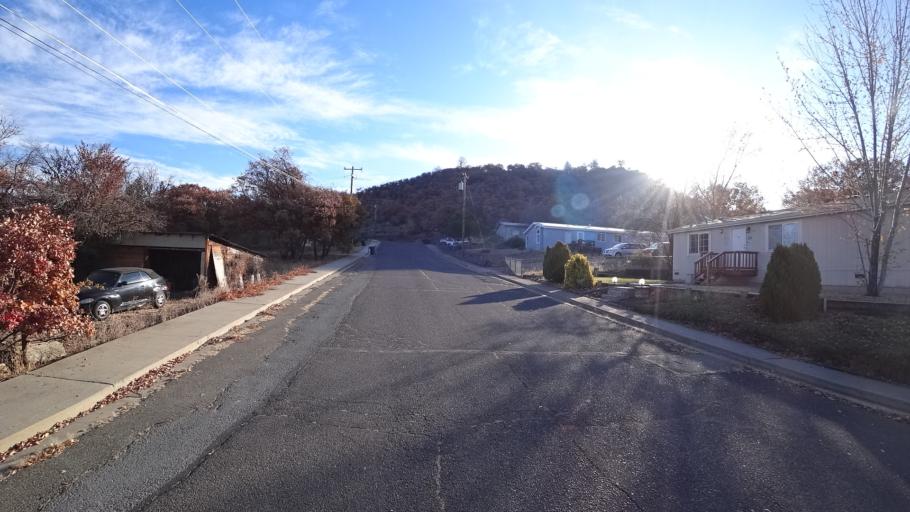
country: US
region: California
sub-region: Siskiyou County
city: Yreka
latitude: 41.7097
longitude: -122.6170
